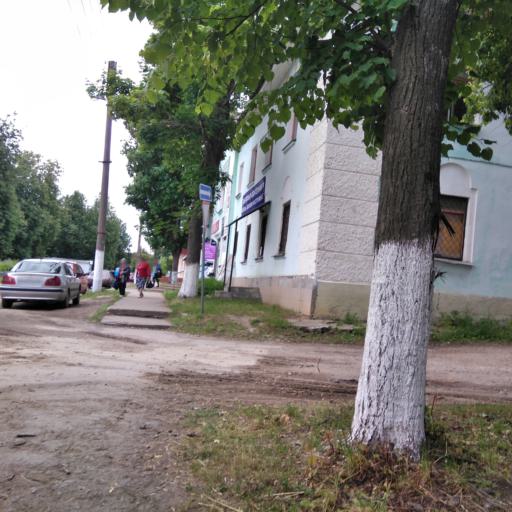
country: RU
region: Tula
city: Lomintsevskiy
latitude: 53.9333
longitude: 37.6256
